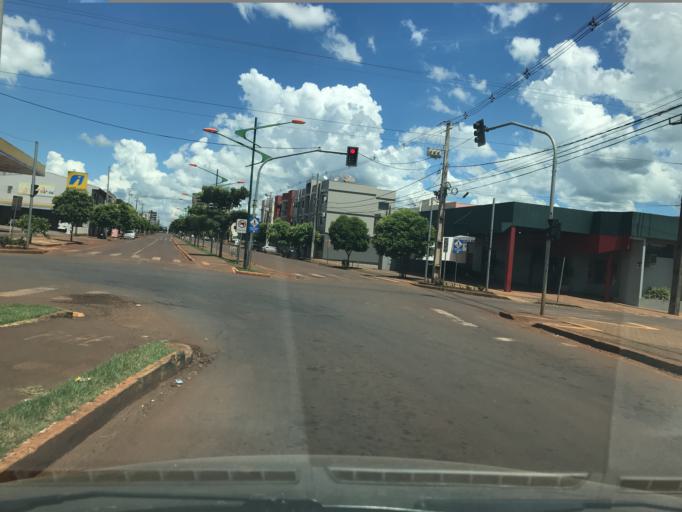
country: BR
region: Parana
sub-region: Palotina
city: Palotina
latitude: -24.2778
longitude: -53.8417
